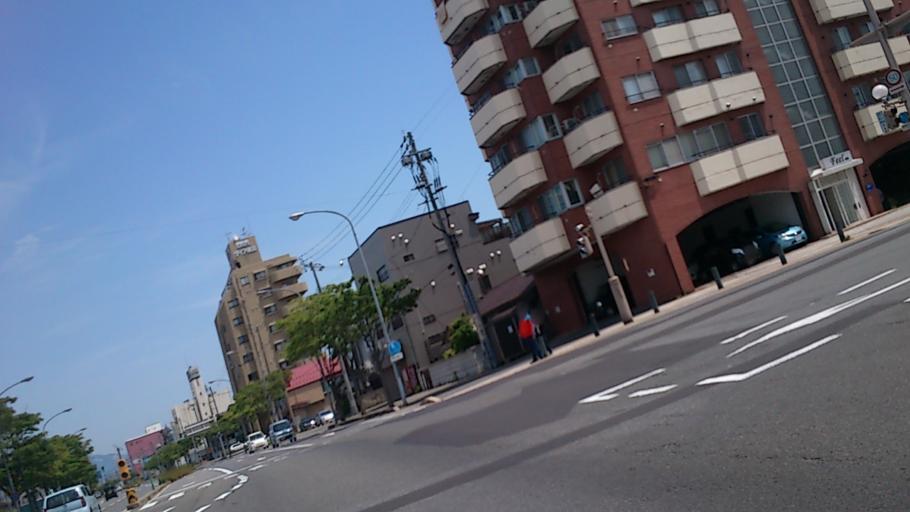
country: JP
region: Aomori
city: Aomori Shi
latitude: 40.8288
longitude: 140.7455
